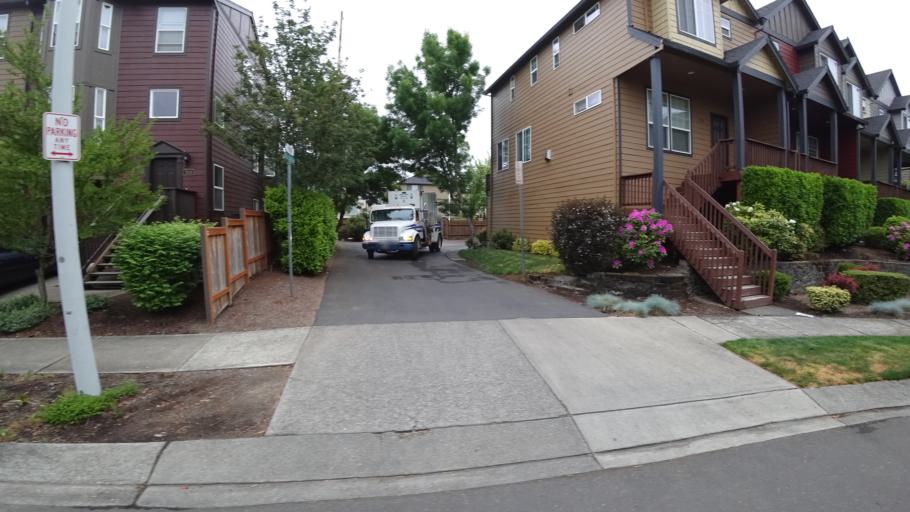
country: US
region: Oregon
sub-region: Washington County
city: Rockcreek
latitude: 45.5227
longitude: -122.9009
